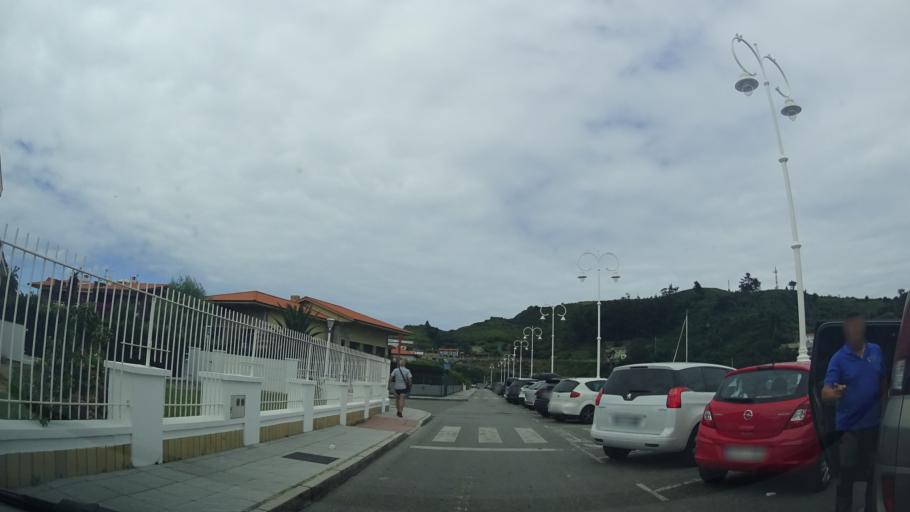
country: ES
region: Asturias
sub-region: Province of Asturias
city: Ribadesella
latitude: 43.4641
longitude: -5.0634
